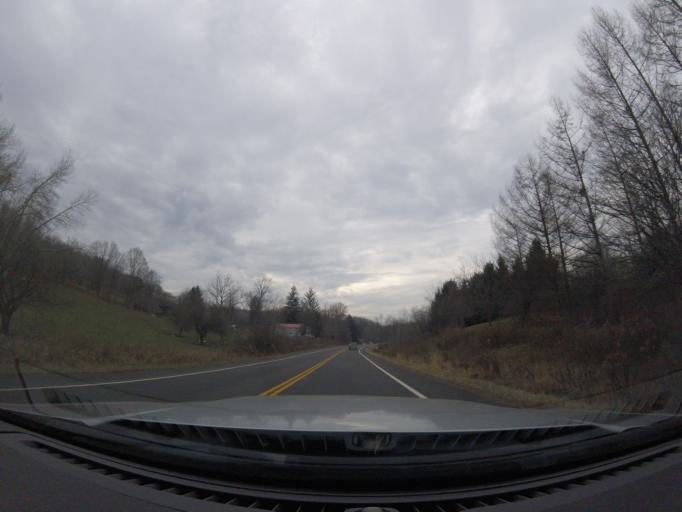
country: US
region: New York
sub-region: Schuyler County
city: Watkins Glen
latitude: 42.4363
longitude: -76.7958
